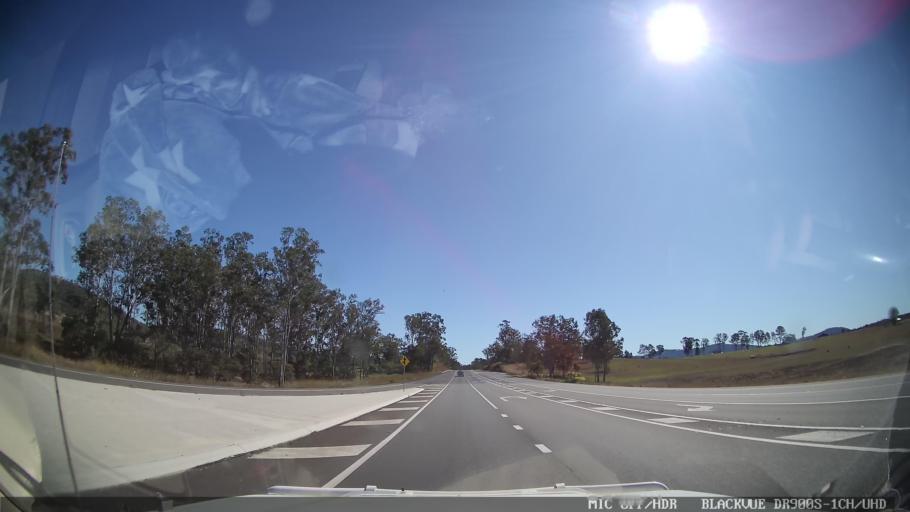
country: AU
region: Queensland
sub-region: Gympie Regional Council
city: Gympie
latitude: -26.0346
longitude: 152.5678
